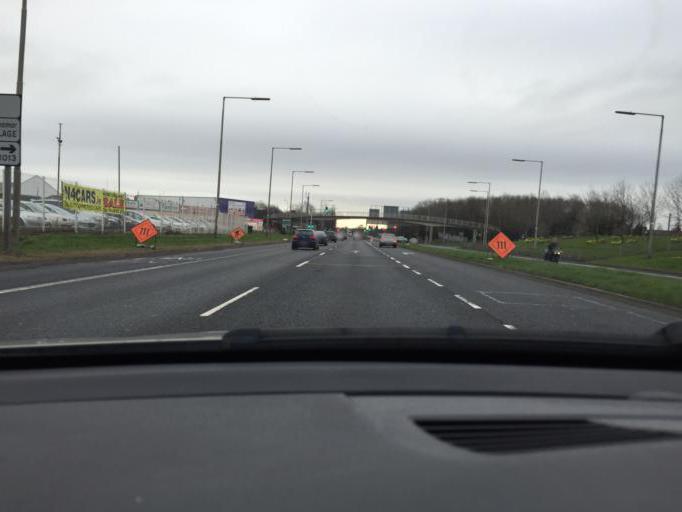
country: IE
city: Palmerstown
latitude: 53.3556
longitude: -6.3744
